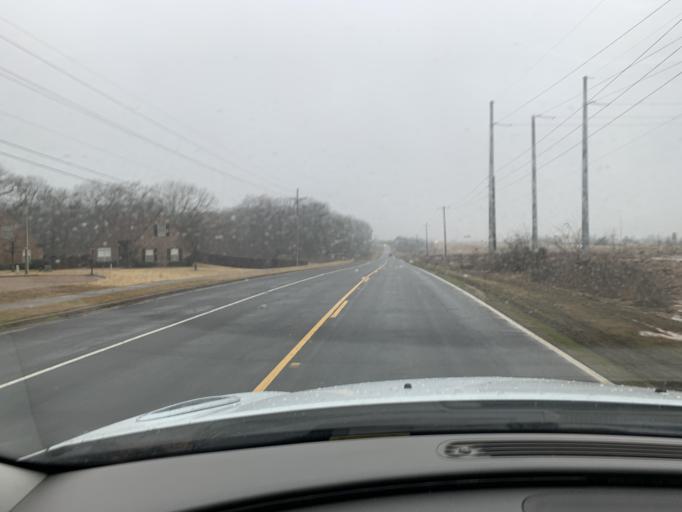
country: US
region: Mississippi
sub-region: De Soto County
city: Hernando
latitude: 34.8605
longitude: -89.9757
